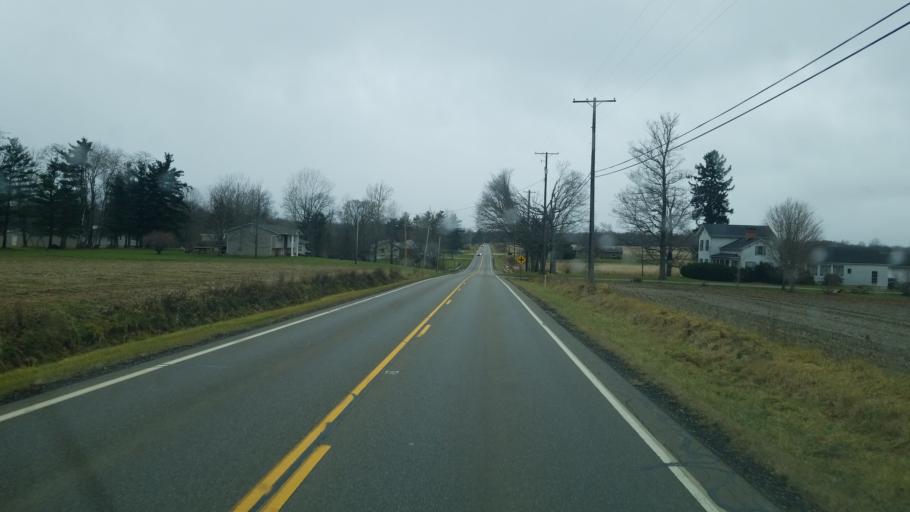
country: US
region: Ohio
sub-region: Ashtabula County
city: Jefferson
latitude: 41.7676
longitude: -80.8301
